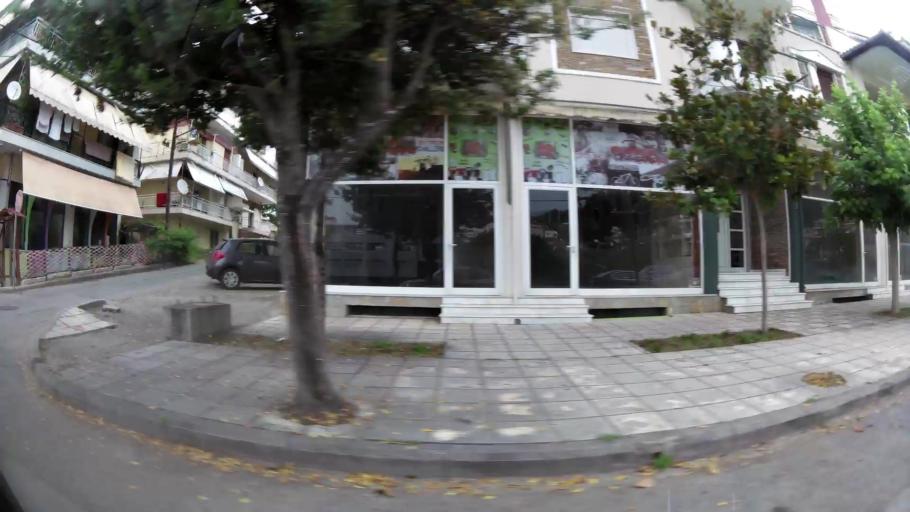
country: GR
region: Central Macedonia
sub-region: Nomos Imathias
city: Veroia
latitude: 40.5255
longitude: 22.1978
